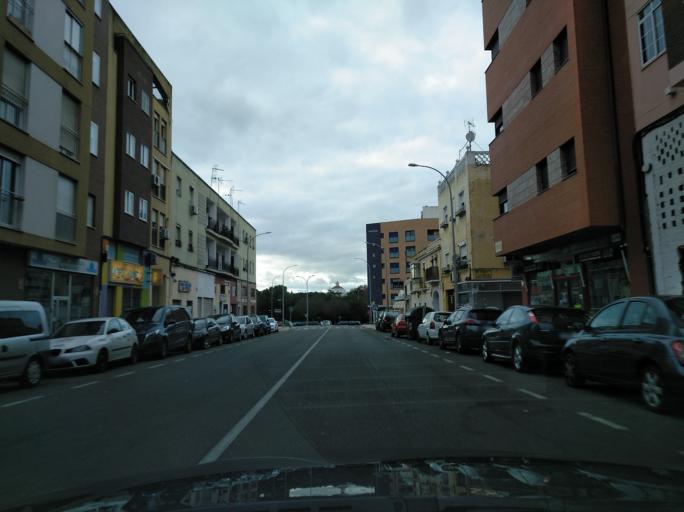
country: ES
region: Extremadura
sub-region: Provincia de Badajoz
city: Badajoz
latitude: 38.8772
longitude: -6.9601
